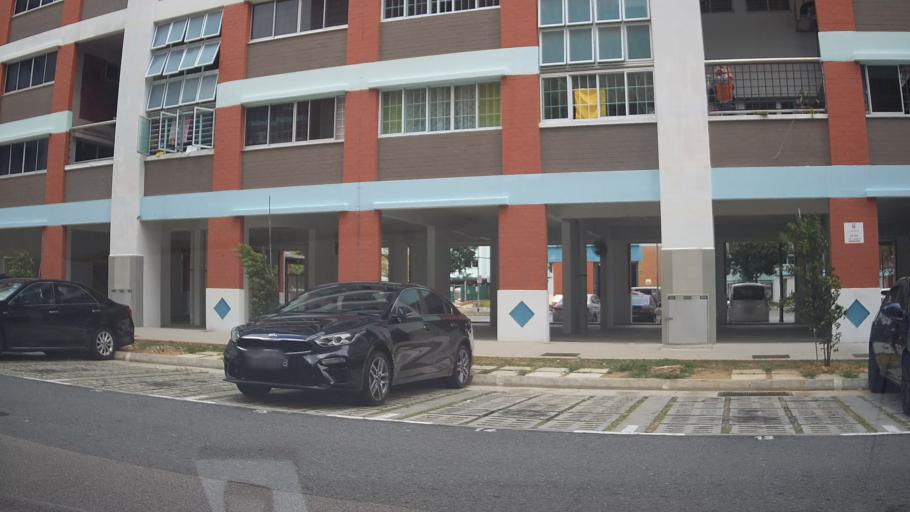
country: SG
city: Singapore
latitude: 1.3487
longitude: 103.9322
